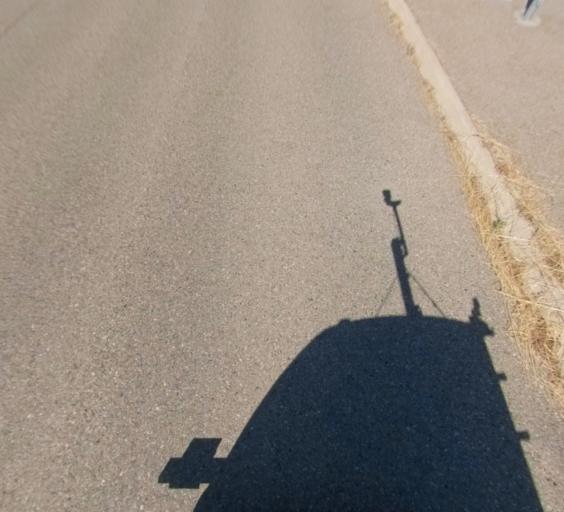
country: US
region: California
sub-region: Fresno County
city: Clovis
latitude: 36.8927
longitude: -119.7944
